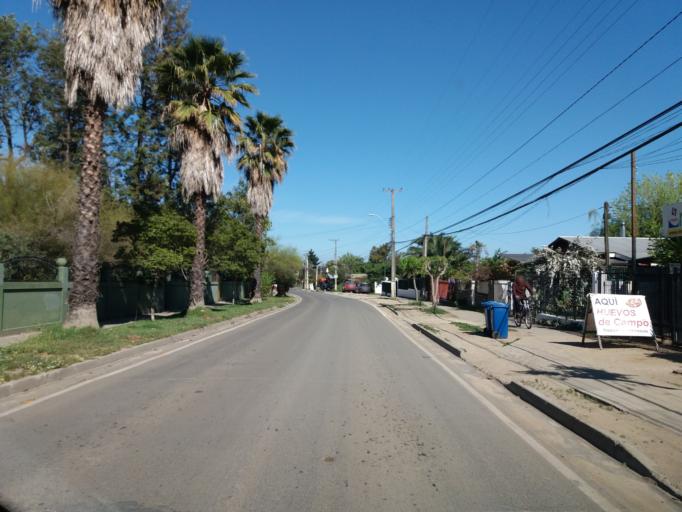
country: CL
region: Valparaiso
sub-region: Provincia de Marga Marga
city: Limache
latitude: -32.9939
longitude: -71.1713
